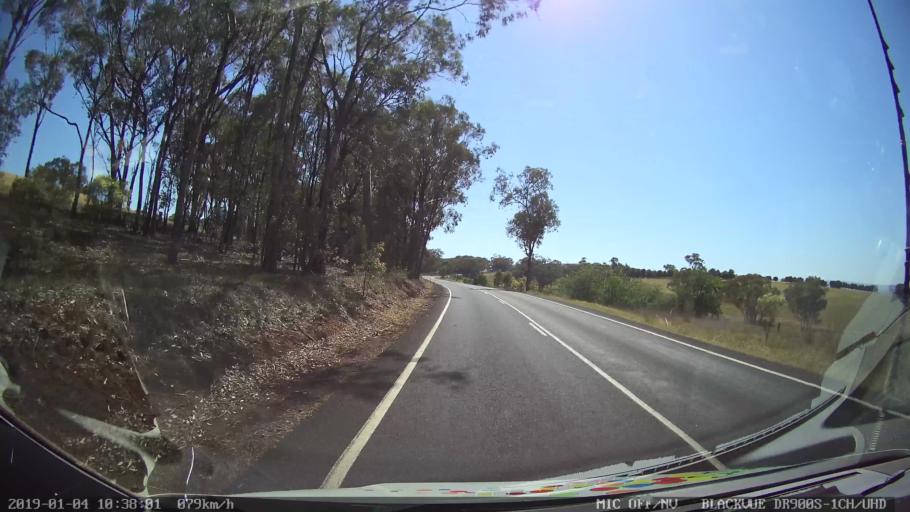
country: AU
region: New South Wales
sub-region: Cabonne
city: Molong
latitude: -33.2946
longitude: 148.7032
